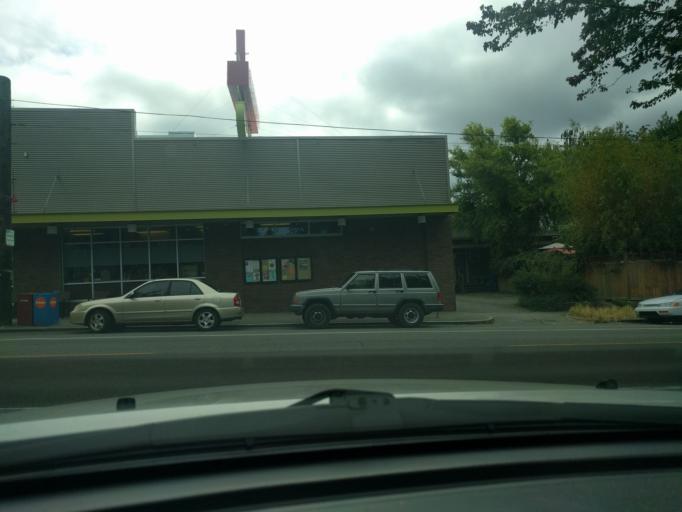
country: US
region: Washington
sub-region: King County
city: Seattle
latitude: 47.6605
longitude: -122.3502
